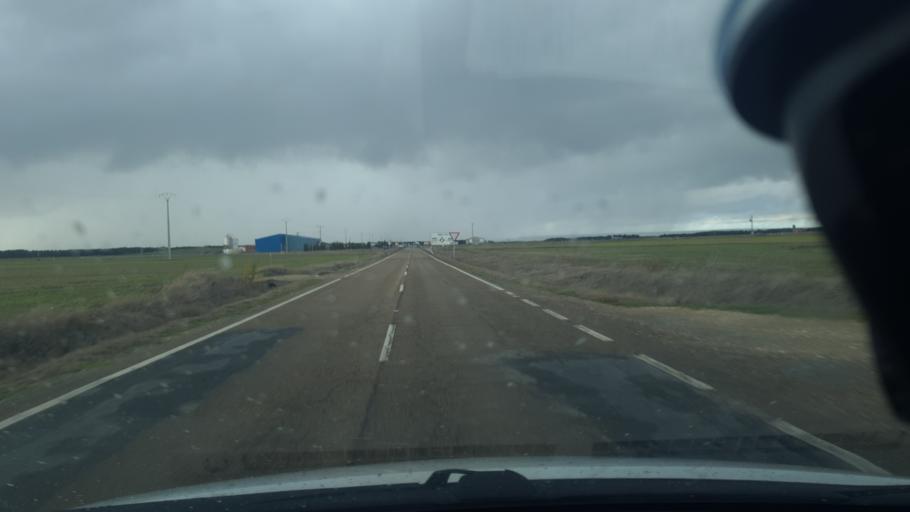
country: ES
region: Castille and Leon
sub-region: Provincia de Segovia
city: Chane
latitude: 41.3175
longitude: -4.3828
